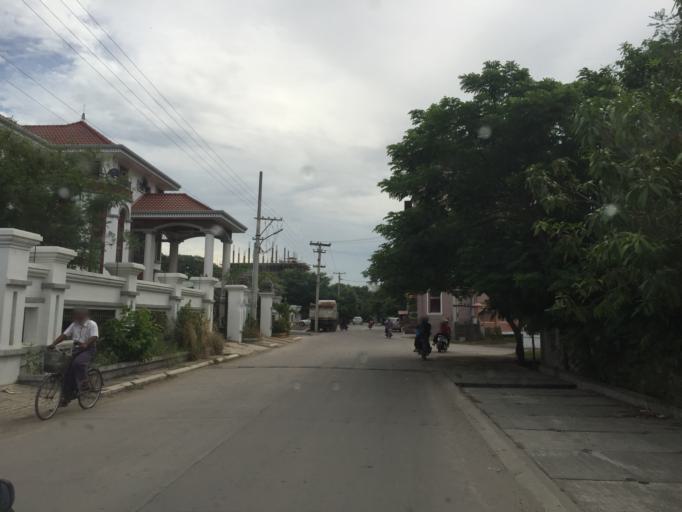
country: MM
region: Mandalay
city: Mandalay
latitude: 21.9698
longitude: 96.1064
